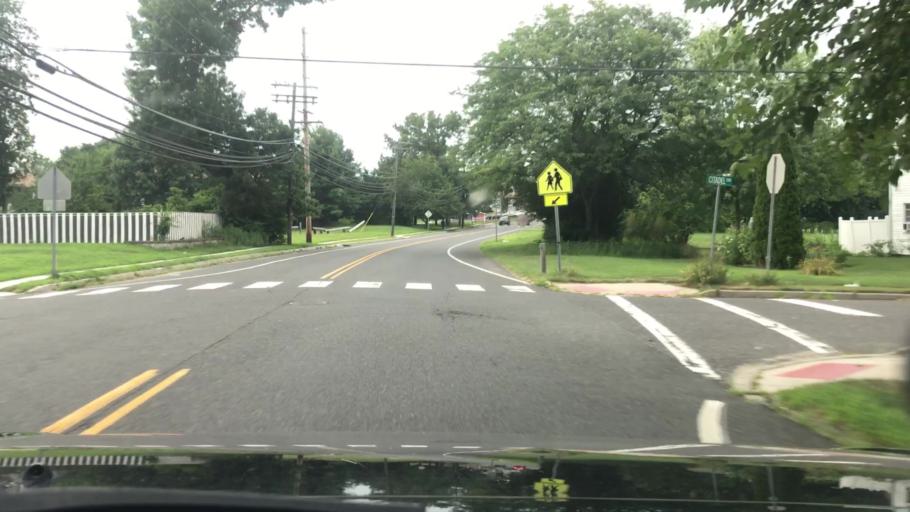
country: US
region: New Jersey
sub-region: Ocean County
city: Lakewood
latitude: 40.1219
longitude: -74.2541
